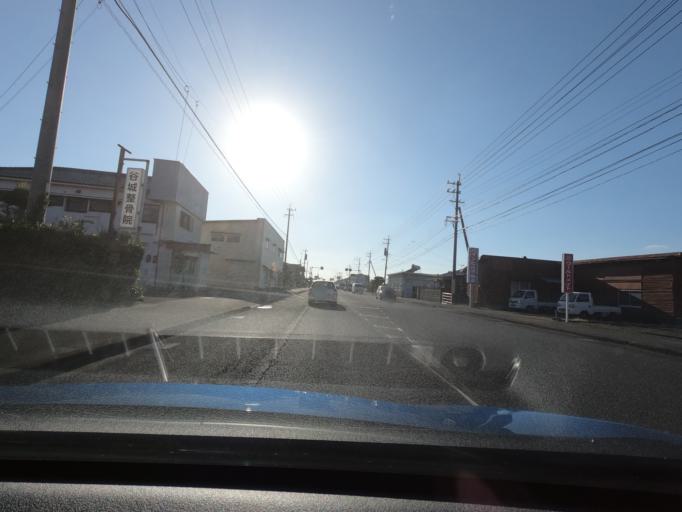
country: JP
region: Kagoshima
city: Izumi
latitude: 32.1136
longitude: 130.3333
